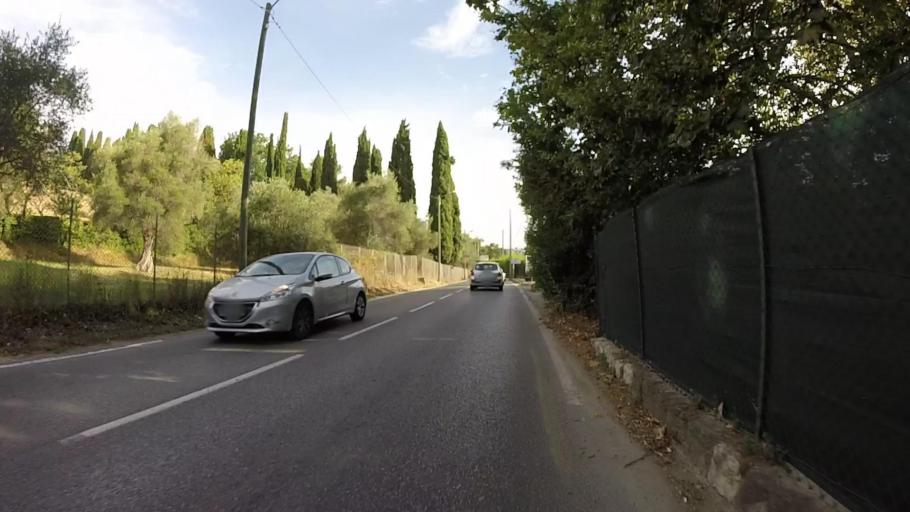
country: FR
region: Provence-Alpes-Cote d'Azur
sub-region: Departement des Alpes-Maritimes
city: Biot
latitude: 43.6135
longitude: 7.1089
